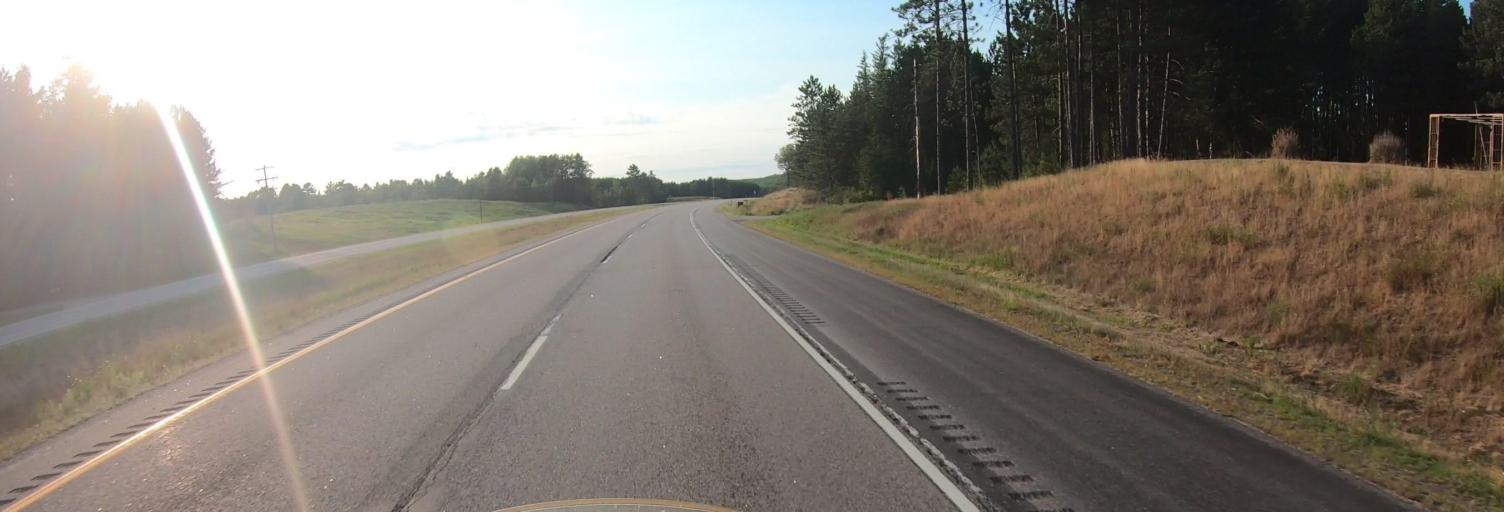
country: US
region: Minnesota
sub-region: Saint Louis County
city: Mountain Iron
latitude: 47.6721
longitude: -92.6323
